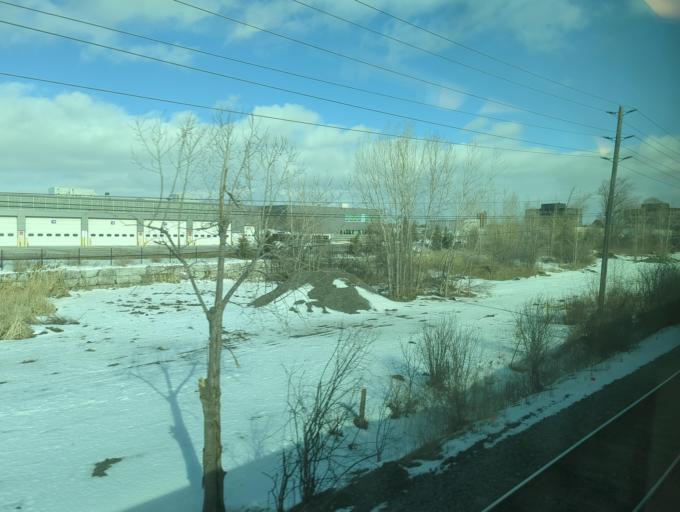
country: CA
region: Ontario
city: Oakville
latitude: 43.4381
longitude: -79.7000
